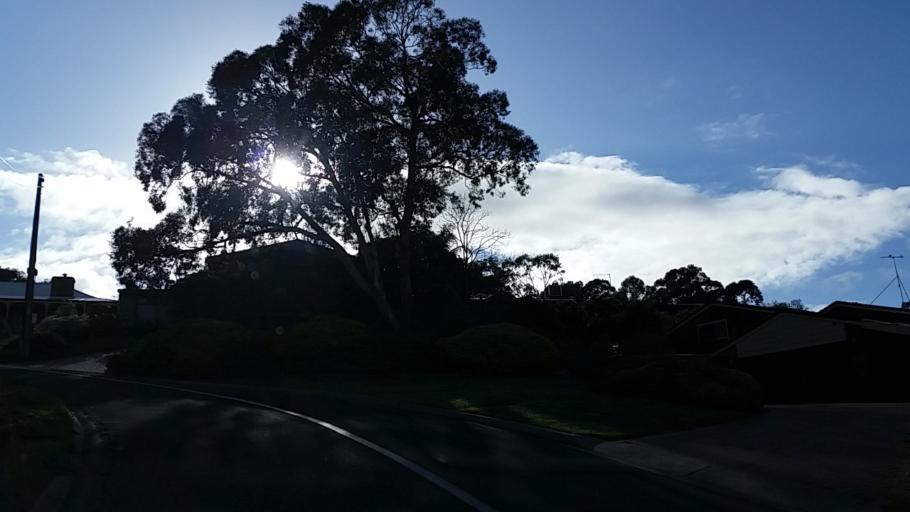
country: AU
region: South Australia
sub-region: Marion
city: Clovelly Park
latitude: -35.0109
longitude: 138.5909
